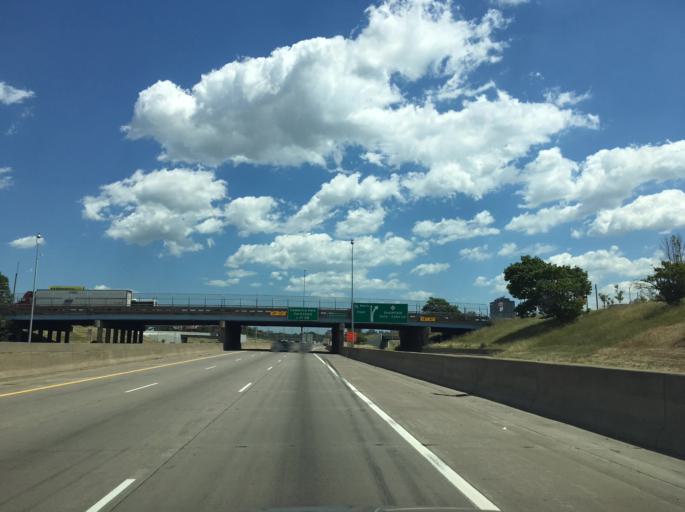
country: US
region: Michigan
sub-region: Wayne County
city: Detroit
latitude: 42.3329
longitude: -83.0743
